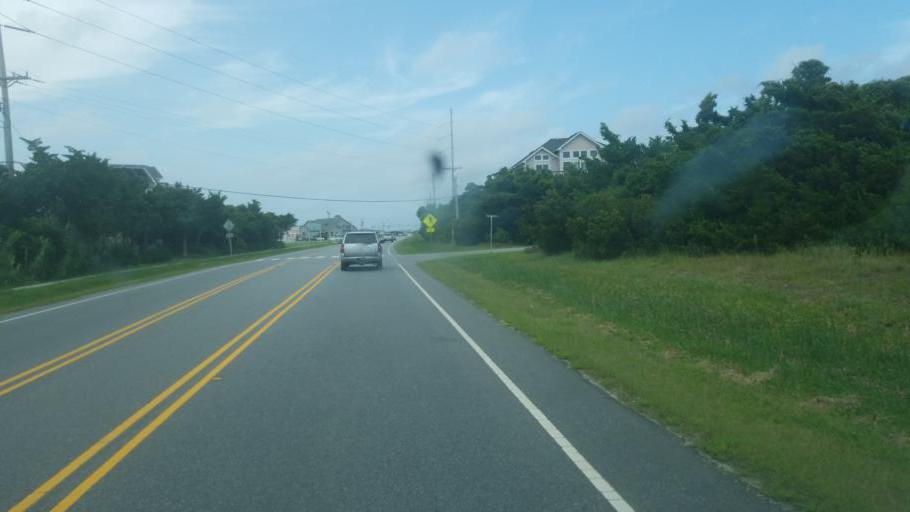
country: US
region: North Carolina
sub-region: Dare County
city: Buxton
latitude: 35.3302
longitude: -75.5076
